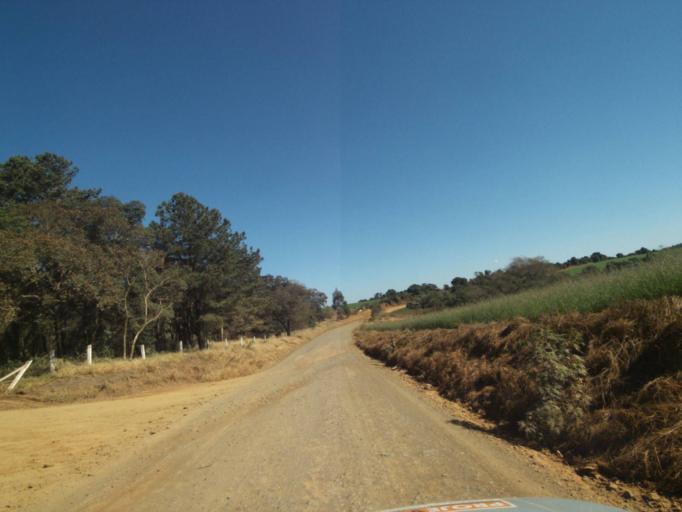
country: BR
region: Parana
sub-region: Reserva
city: Reserva
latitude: -24.6275
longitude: -50.6214
